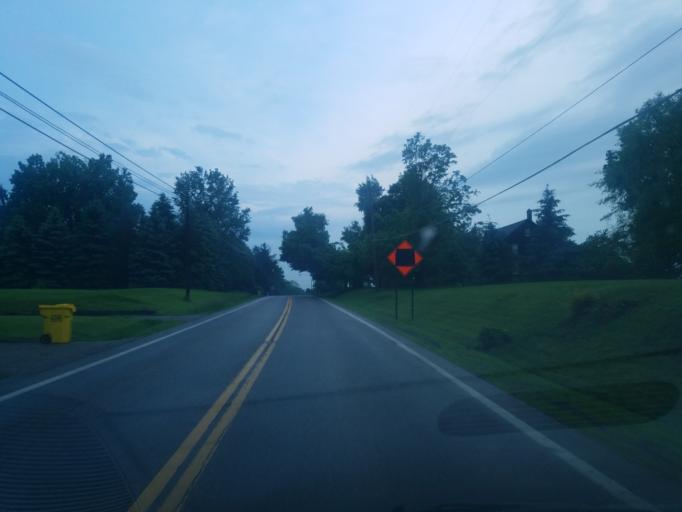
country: US
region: Ohio
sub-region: Columbiana County
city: Salem
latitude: 40.8773
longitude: -80.8821
